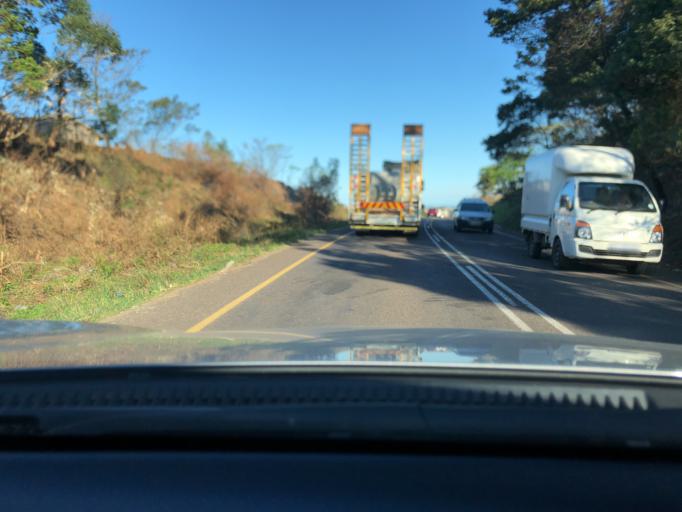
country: ZA
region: KwaZulu-Natal
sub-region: eThekwini Metropolitan Municipality
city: Umkomaas
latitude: -29.9973
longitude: 30.7976
